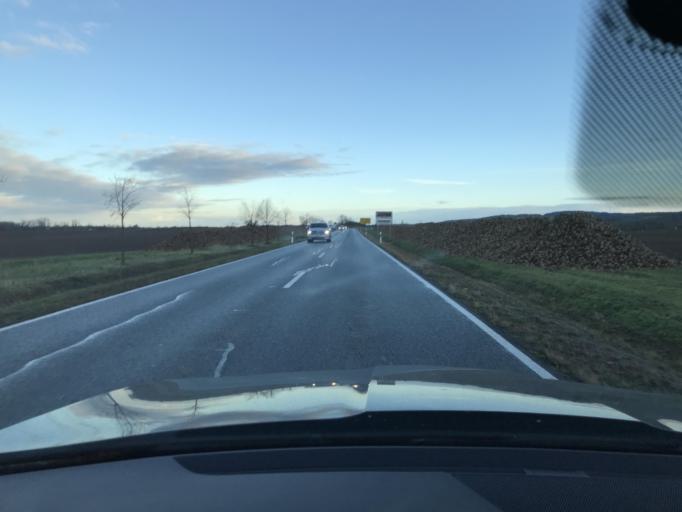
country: DE
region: Saxony-Anhalt
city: Bad Suderode
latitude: 51.7495
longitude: 11.1161
